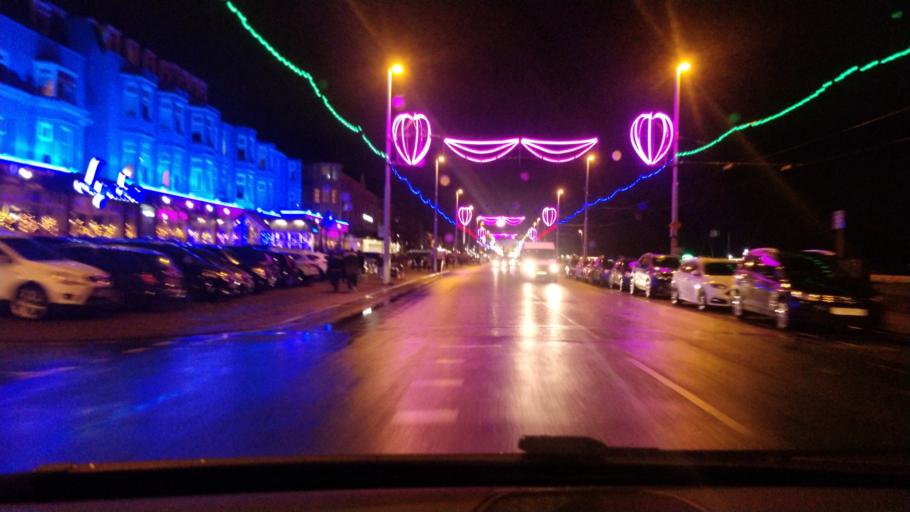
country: GB
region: England
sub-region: Blackpool
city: Blackpool
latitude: 53.8042
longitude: -3.0553
